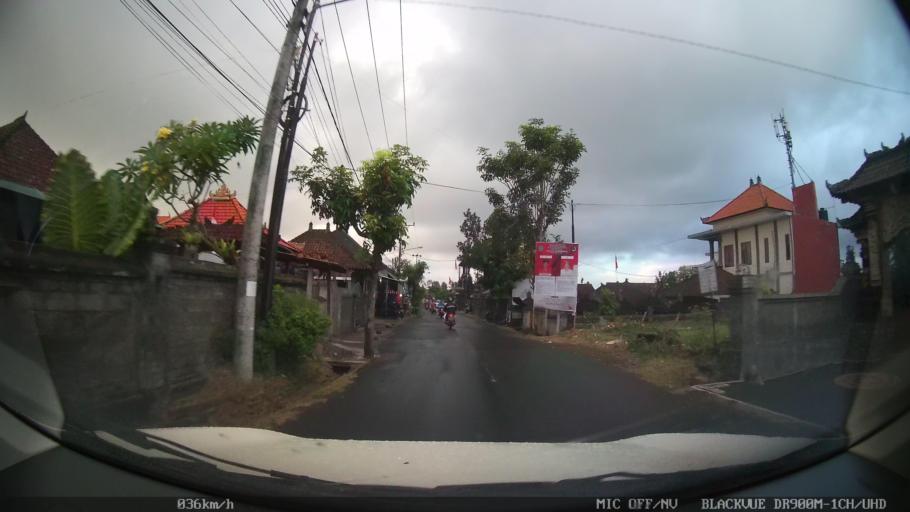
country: ID
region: Bali
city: Banjar Batur
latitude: -8.6081
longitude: 115.2210
